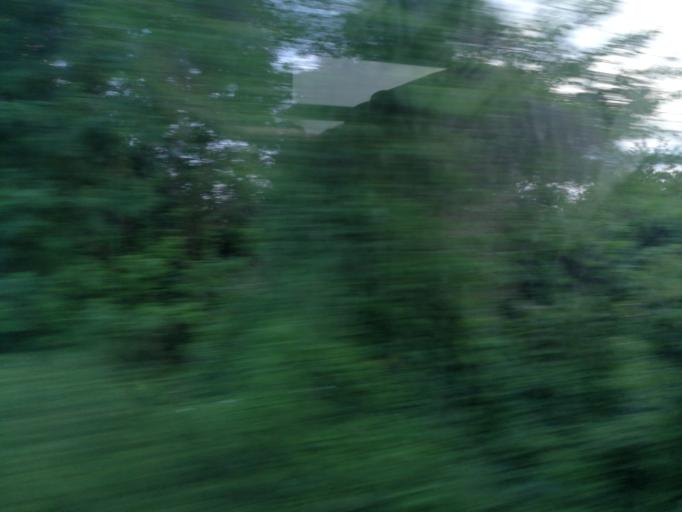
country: RO
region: Dambovita
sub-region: Comuna Contesti
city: Balteni
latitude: 44.6557
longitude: 25.6598
